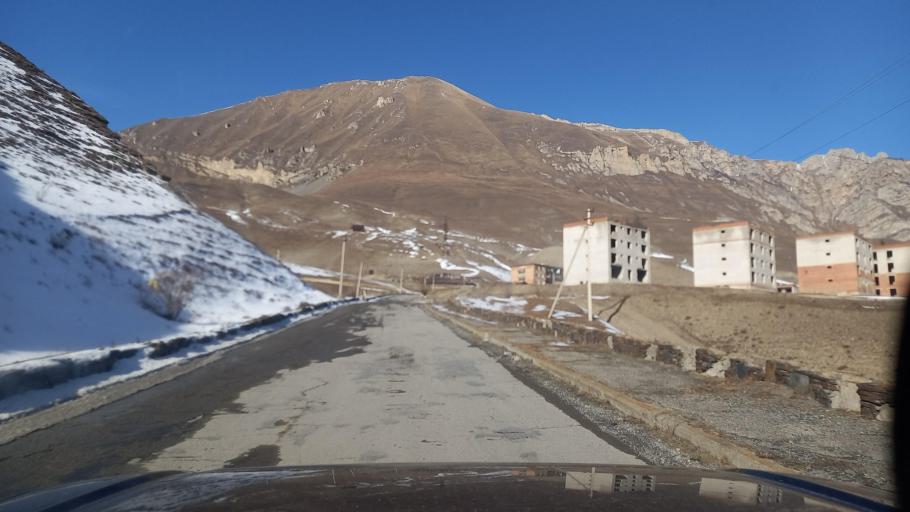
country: RU
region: Ingushetiya
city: Dzhayrakh
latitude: 42.8432
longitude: 44.5109
